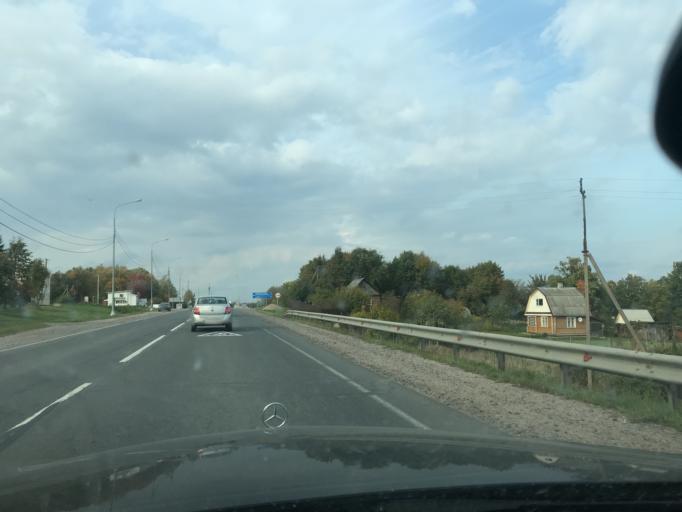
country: RU
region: Pskov
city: Ostrov
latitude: 57.3089
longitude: 28.3663
